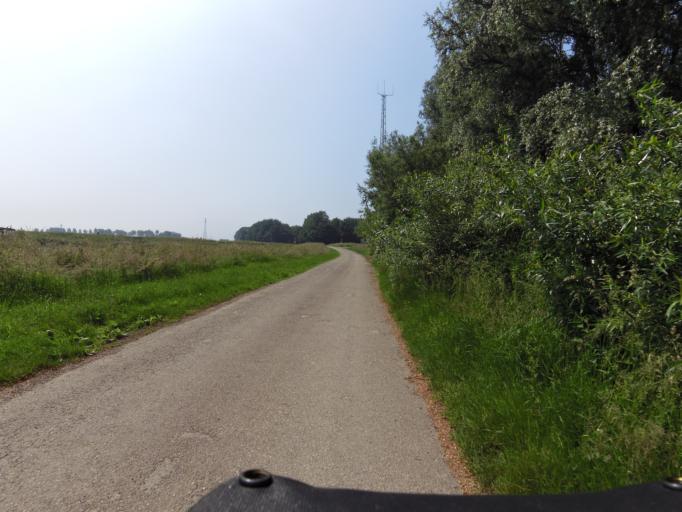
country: NL
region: South Holland
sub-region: Gemeente Maassluis
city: Maassluis
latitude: 51.8710
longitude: 4.2337
